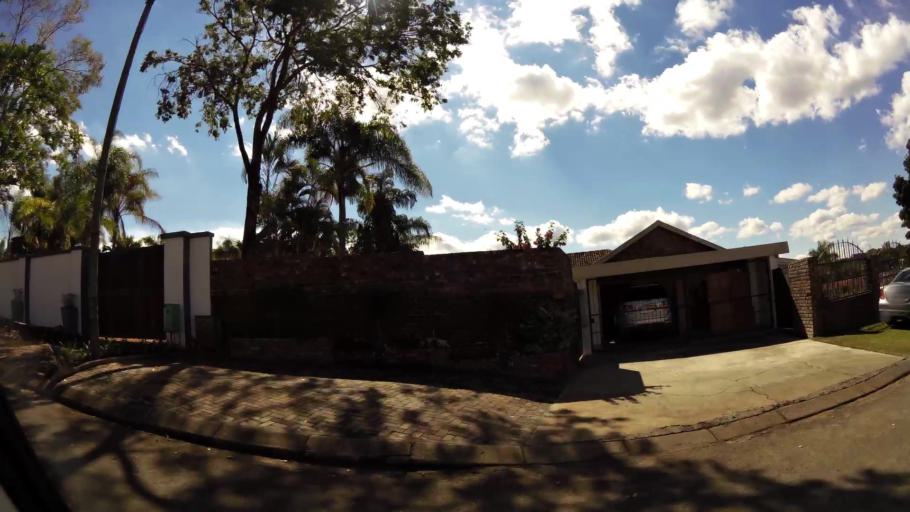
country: ZA
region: Limpopo
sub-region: Mopani District Municipality
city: Tzaneen
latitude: -23.8156
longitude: 30.1579
